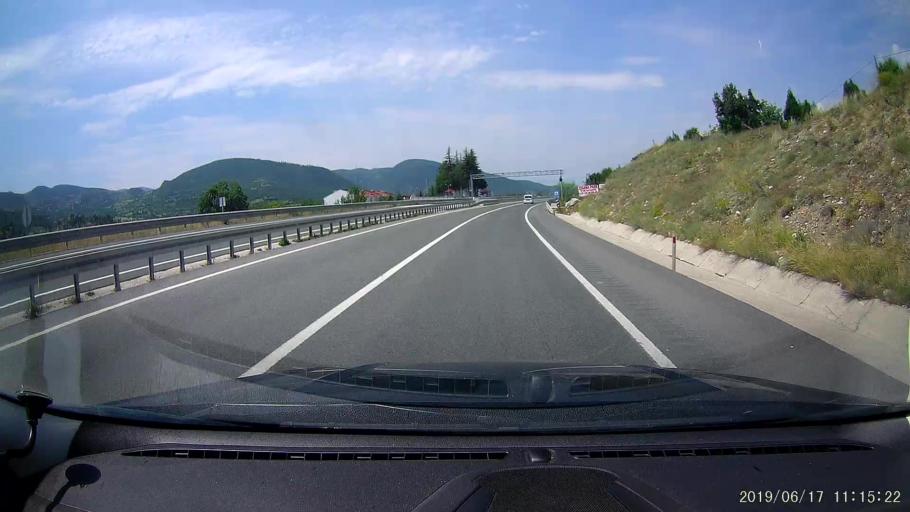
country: TR
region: Kastamonu
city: Tosya
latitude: 40.9519
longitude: 33.9247
